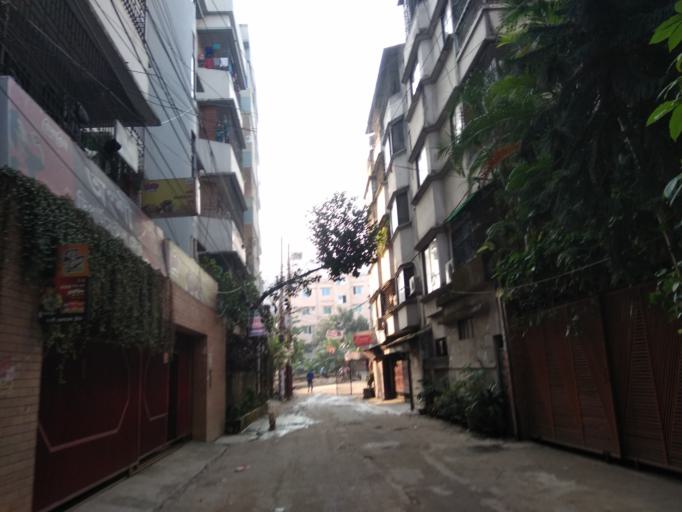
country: BD
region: Dhaka
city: Azimpur
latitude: 23.7605
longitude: 90.3550
